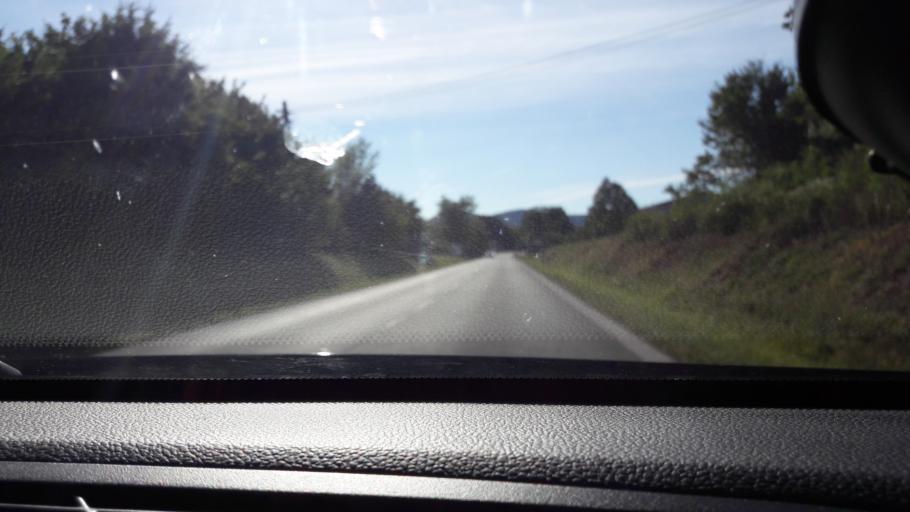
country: SK
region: Kosicky
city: Vinne
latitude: 48.8104
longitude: 22.0327
